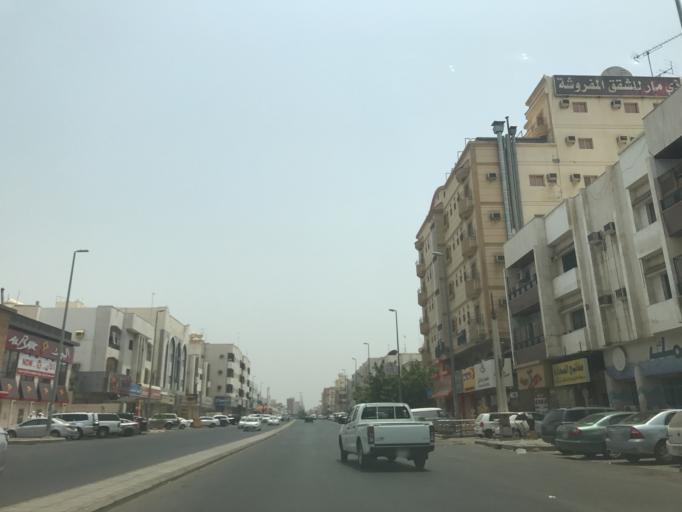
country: SA
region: Makkah
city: Jeddah
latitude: 21.5869
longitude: 39.1581
